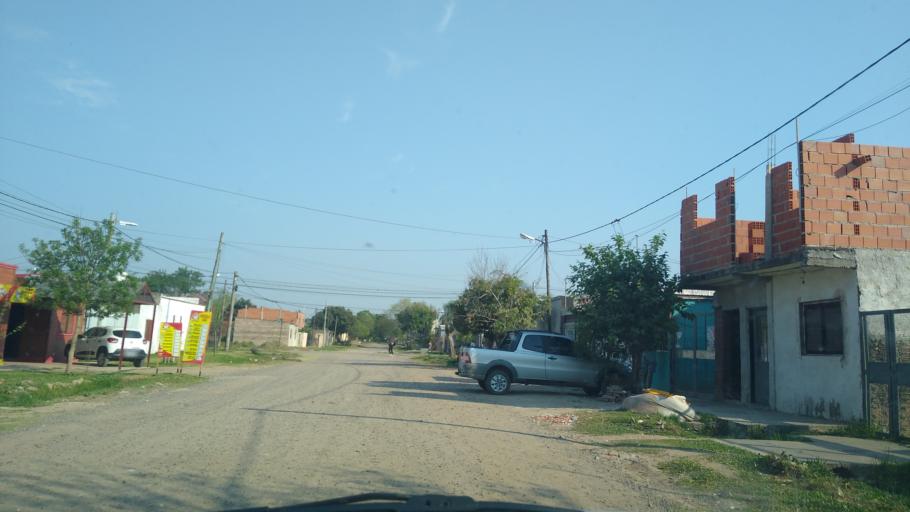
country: AR
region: Chaco
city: Barranqueras
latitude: -27.4763
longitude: -58.9512
